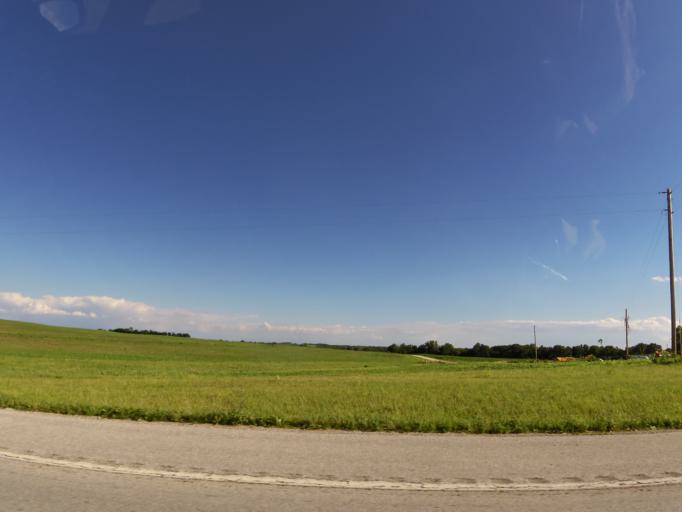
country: US
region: Missouri
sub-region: Marion County
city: Palmyra
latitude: 39.7437
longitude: -91.5035
